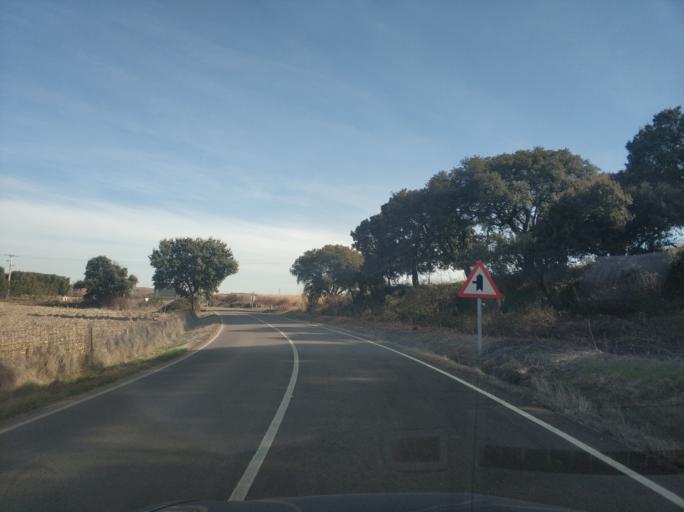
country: ES
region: Castille and Leon
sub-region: Provincia de Salamanca
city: Doninos de Salamanca
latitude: 40.9893
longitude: -5.7310
